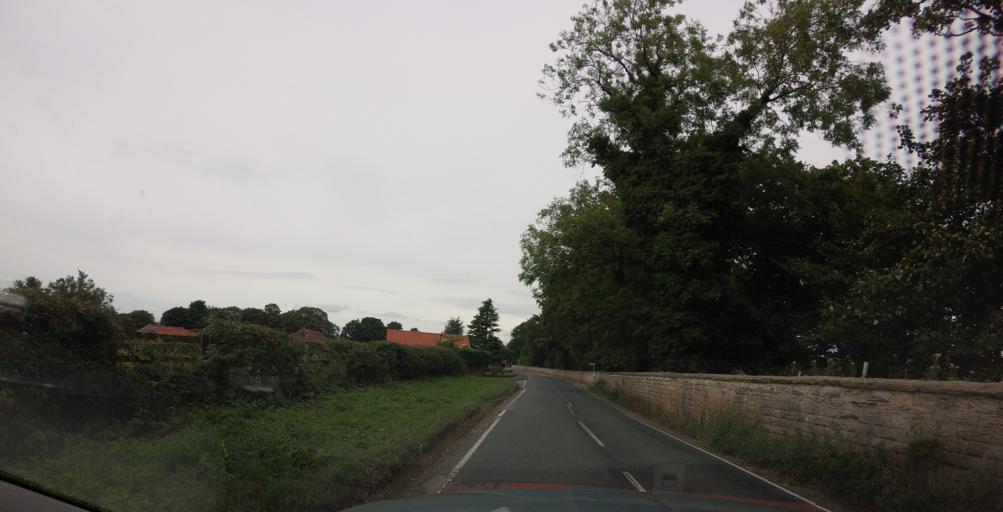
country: GB
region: England
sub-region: North Yorkshire
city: Ripon
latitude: 54.1423
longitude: -1.4959
